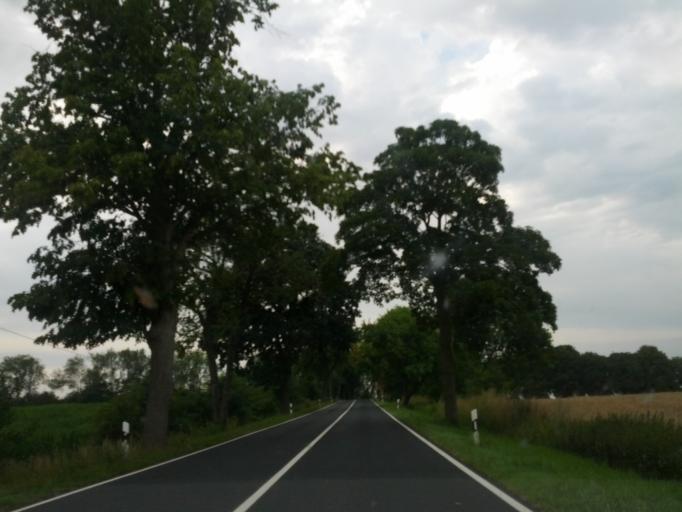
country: DE
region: Mecklenburg-Vorpommern
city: Kropelin
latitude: 54.0095
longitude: 11.8166
